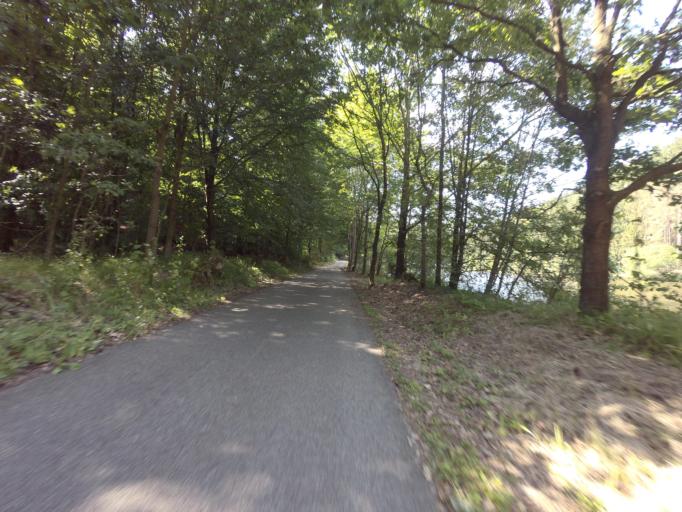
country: CZ
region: Jihocesky
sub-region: Okres Ceske Budejovice
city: Hluboka nad Vltavou
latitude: 49.0701
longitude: 14.4590
